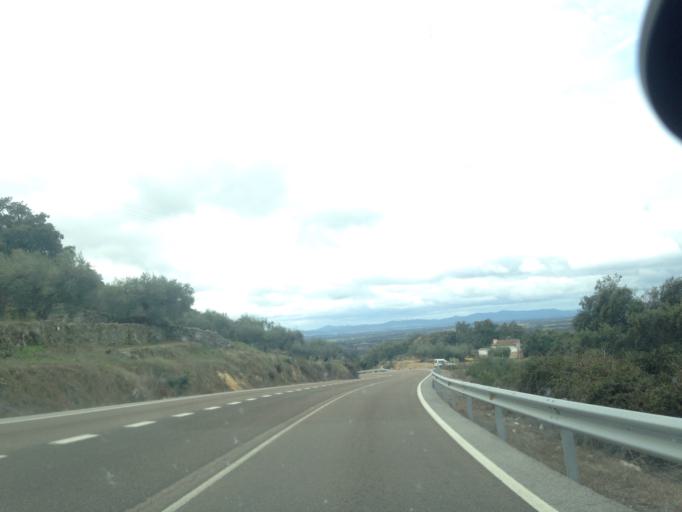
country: ES
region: Extremadura
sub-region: Provincia de Caceres
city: Montanchez
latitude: 39.2316
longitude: -6.1555
